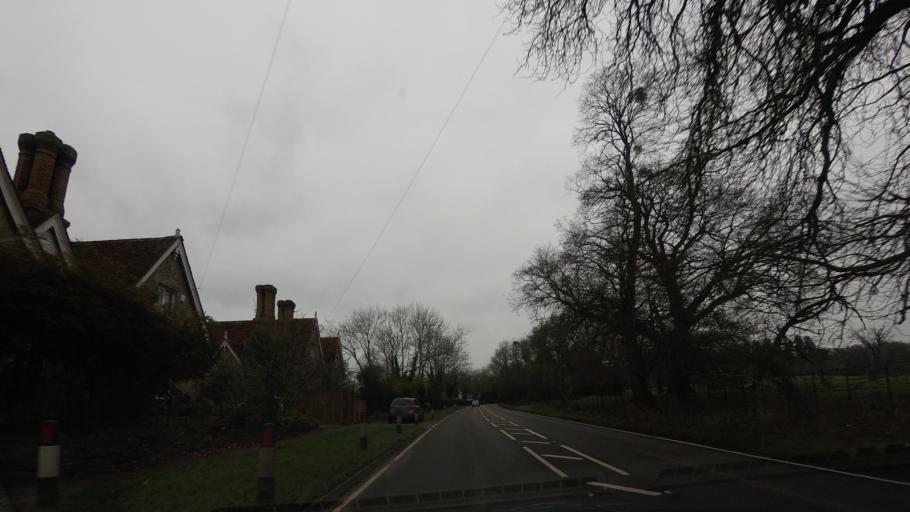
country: GB
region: England
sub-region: Kent
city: Marden
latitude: 51.2179
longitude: 0.5112
